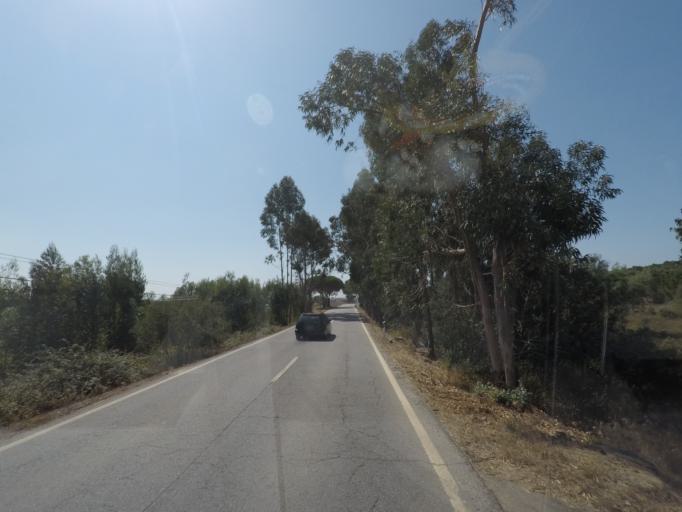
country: PT
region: Beja
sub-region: Odemira
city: Sao Teotonio
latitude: 37.5244
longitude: -8.7004
